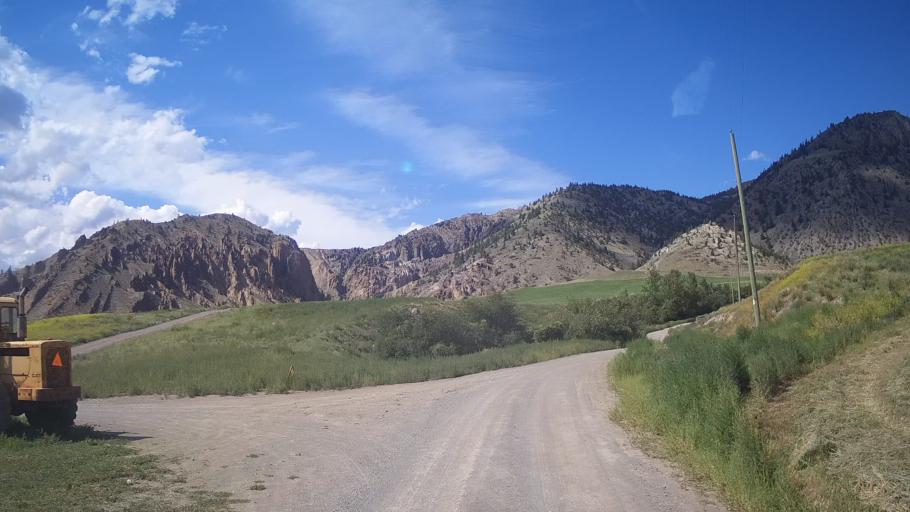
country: CA
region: British Columbia
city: Lillooet
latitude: 51.1886
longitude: -122.1191
